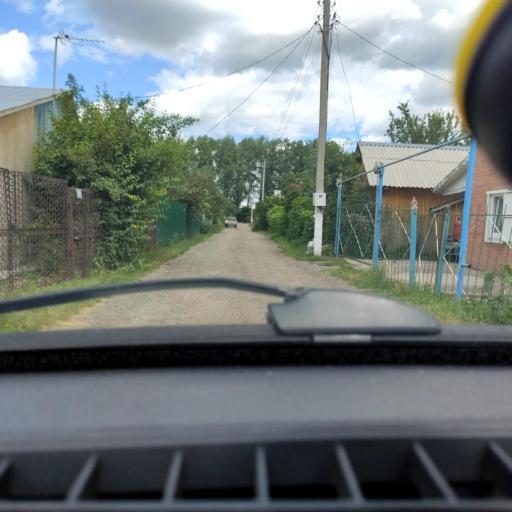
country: RU
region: Samara
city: Podstepki
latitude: 53.6057
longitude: 49.2266
